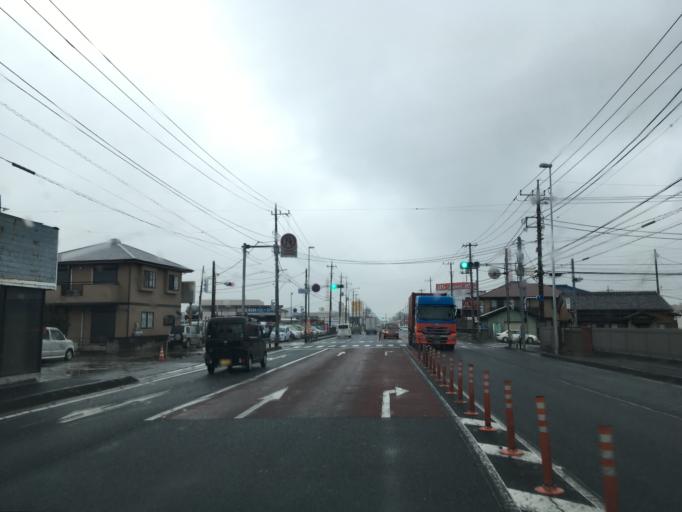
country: JP
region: Saitama
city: Koshigaya
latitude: 35.8855
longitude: 139.7733
